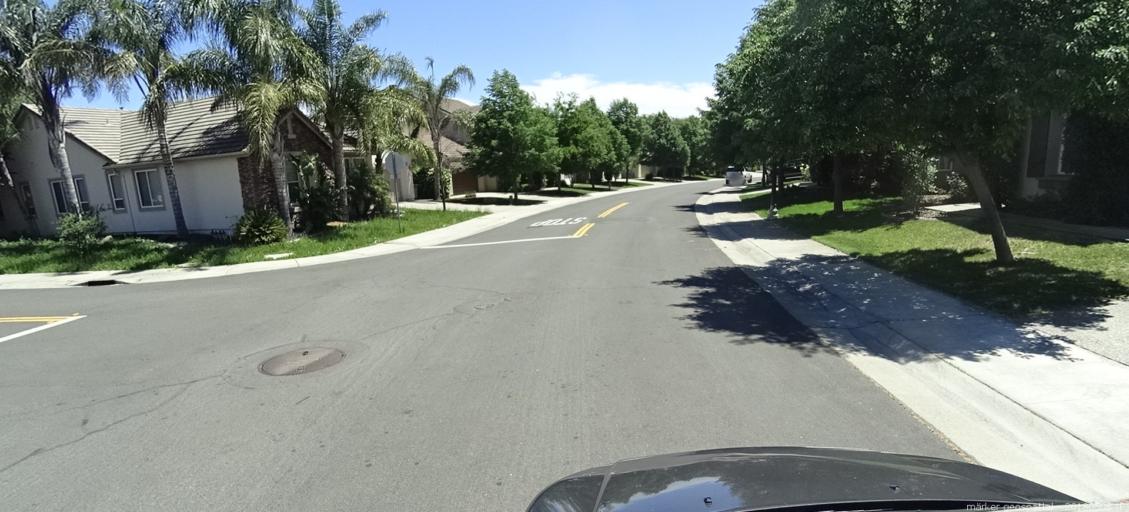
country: US
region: California
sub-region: Sacramento County
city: Elverta
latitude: 38.6777
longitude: -121.5227
